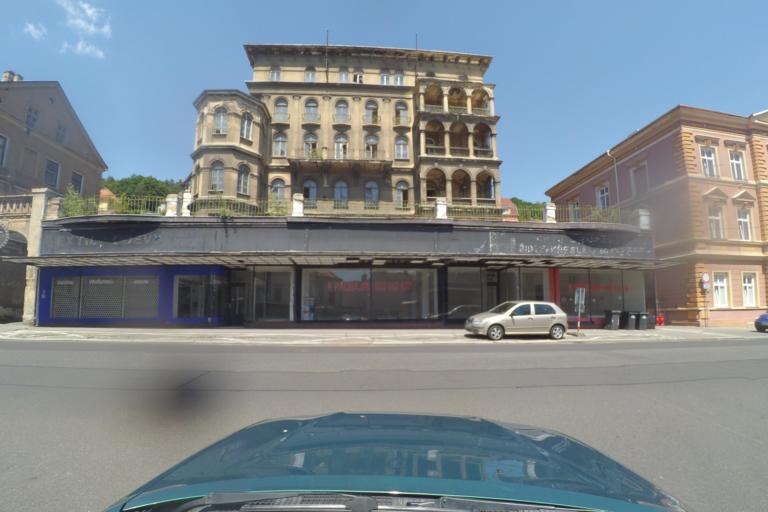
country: CZ
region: Ustecky
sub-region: Okres Decin
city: Decin
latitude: 50.7758
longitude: 14.1953
